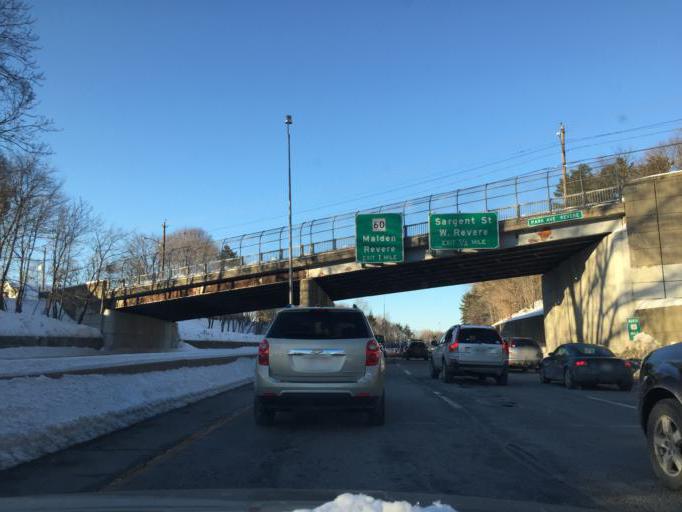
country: US
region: Massachusetts
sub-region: Suffolk County
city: Revere
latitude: 42.4147
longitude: -71.0312
